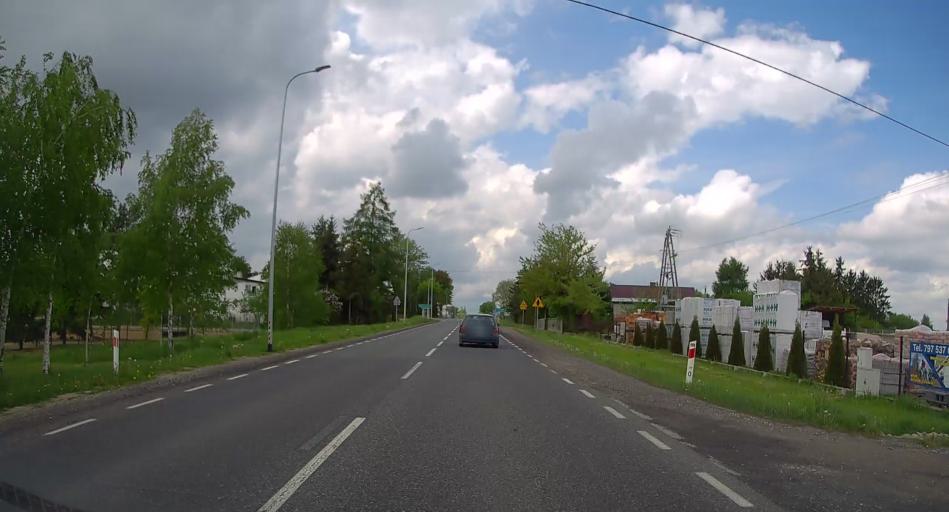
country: PL
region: Masovian Voivodeship
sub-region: Powiat plonski
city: Zaluski
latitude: 52.4441
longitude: 20.5266
